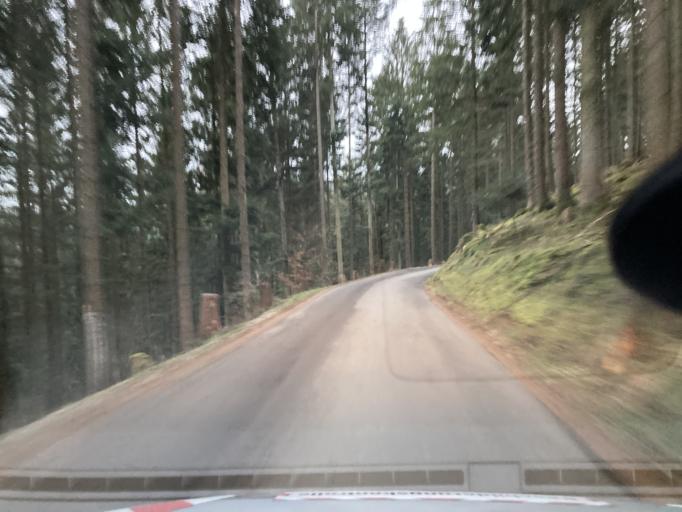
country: DE
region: Baden-Wuerttemberg
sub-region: Karlsruhe Region
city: Neubulach
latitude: 48.6685
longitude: 8.6525
